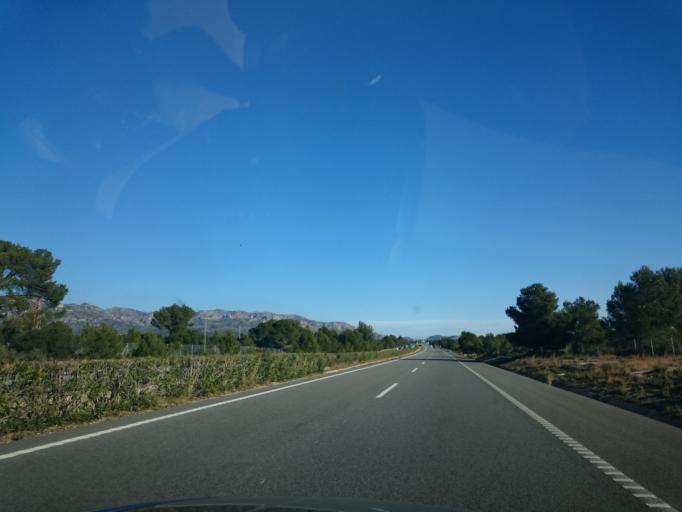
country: ES
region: Catalonia
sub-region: Provincia de Tarragona
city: l'Ametlla de Mar
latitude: 40.9116
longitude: 0.8242
